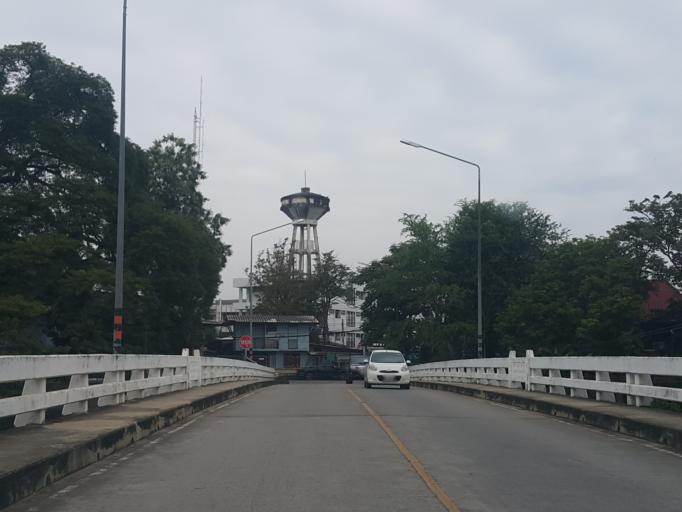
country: TH
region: Lampang
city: Lampang
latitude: 18.2936
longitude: 99.5033
